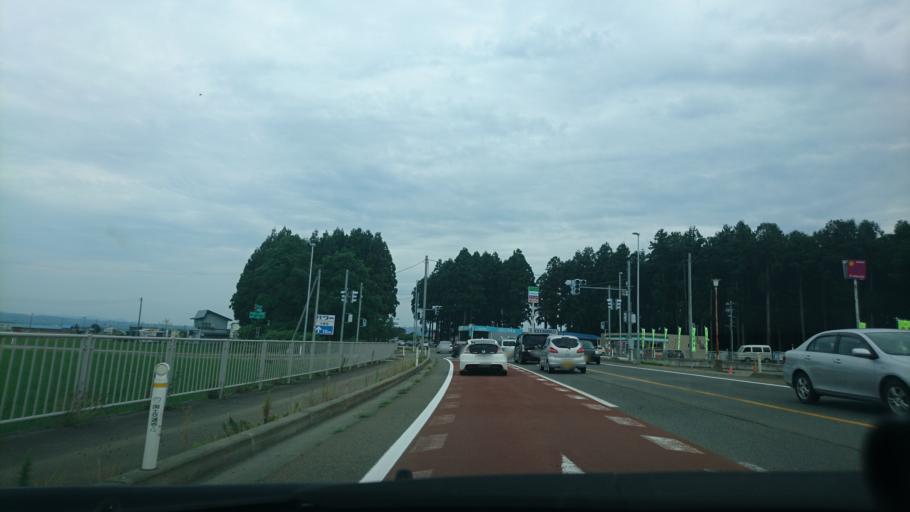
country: JP
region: Akita
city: Omagari
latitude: 39.4148
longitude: 140.5512
